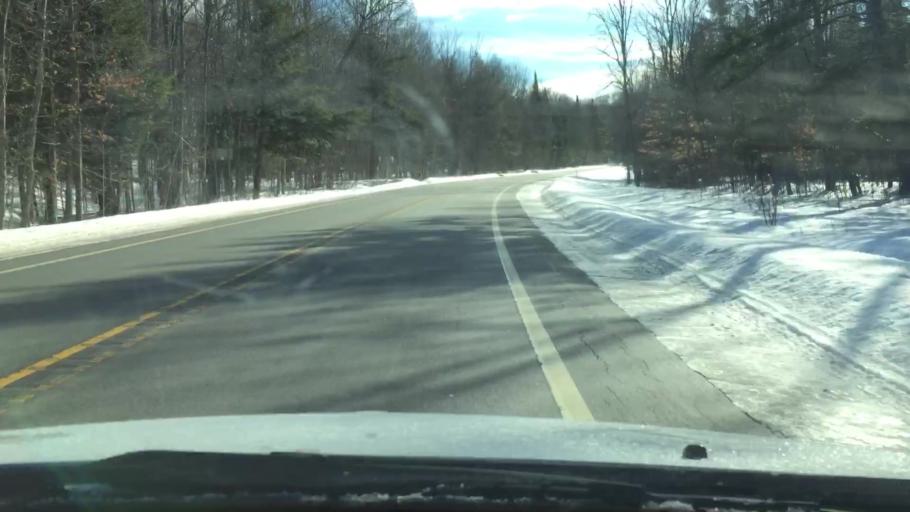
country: US
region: Michigan
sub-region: Antrim County
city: Mancelona
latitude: 45.0049
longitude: -85.0629
